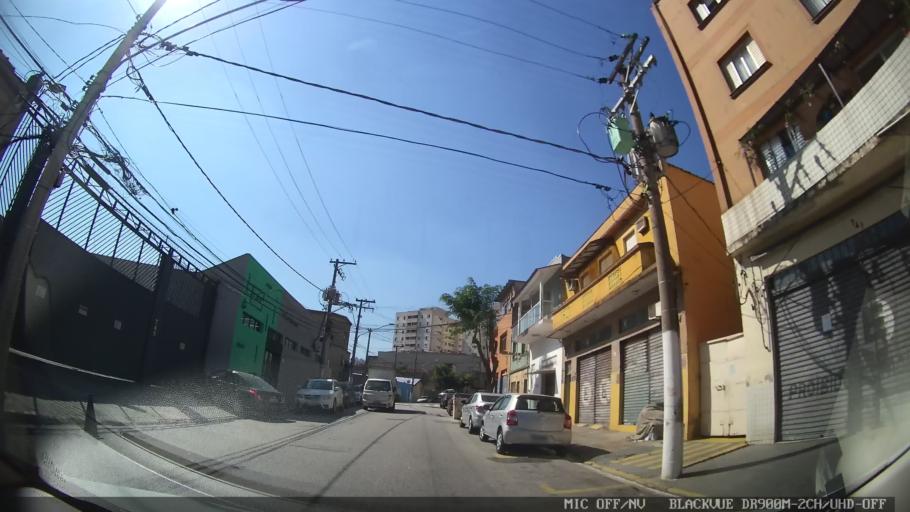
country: BR
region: Sao Paulo
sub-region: Sao Paulo
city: Sao Paulo
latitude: -23.5079
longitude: -46.6594
